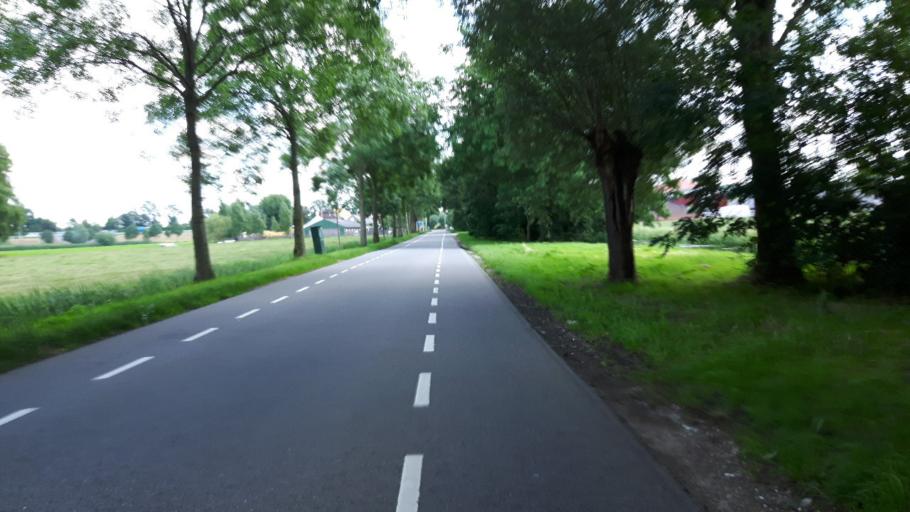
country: NL
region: South Holland
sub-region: Bodegraven-Reeuwijk
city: Bodegraven
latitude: 52.0808
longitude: 4.7330
